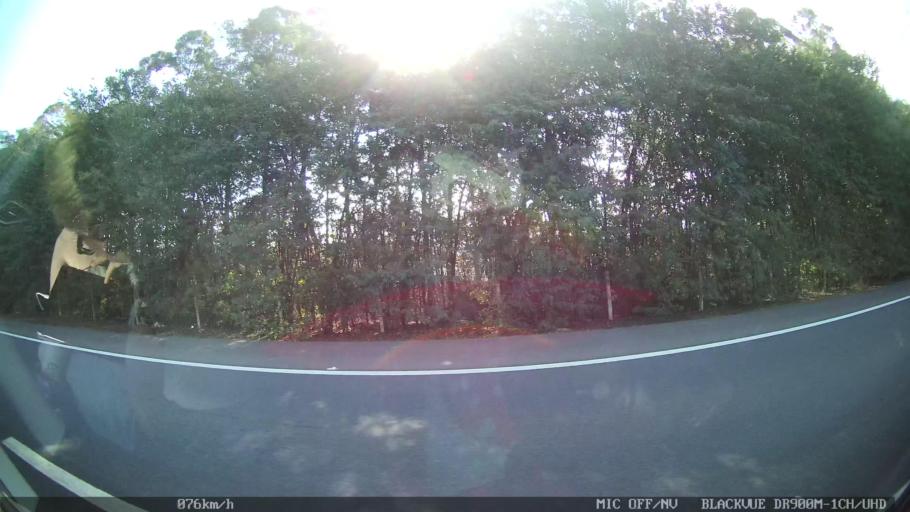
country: BR
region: Sao Paulo
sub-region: Iracemapolis
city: Iracemapolis
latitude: -22.6574
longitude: -47.5221
